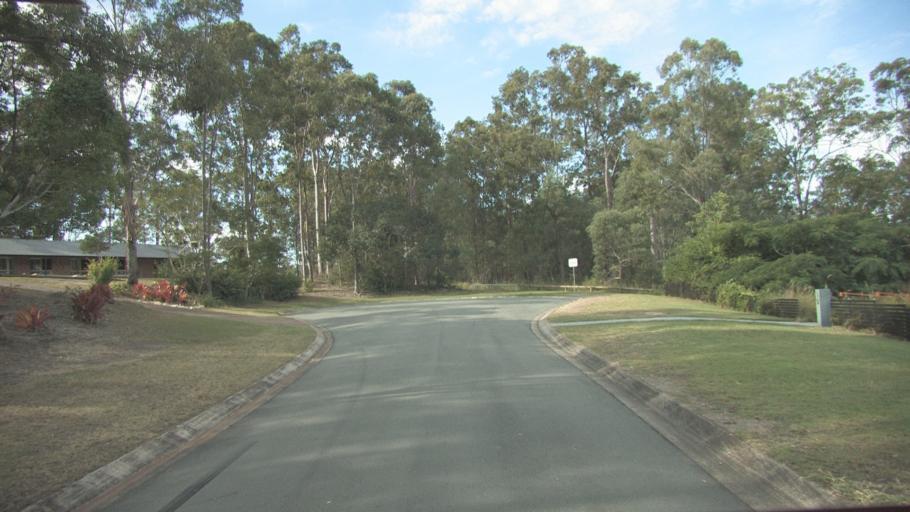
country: AU
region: Queensland
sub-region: Logan
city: Windaroo
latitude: -27.7607
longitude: 153.1945
